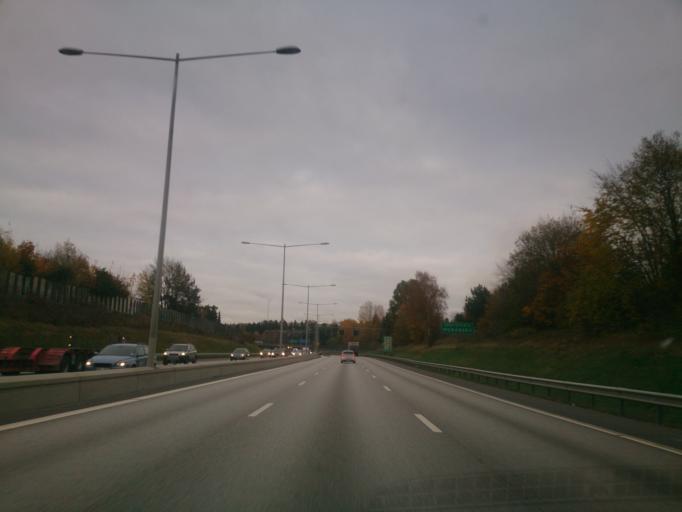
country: SE
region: Stockholm
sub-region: Sodertalje Kommun
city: Soedertaelje
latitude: 59.1894
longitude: 17.6495
